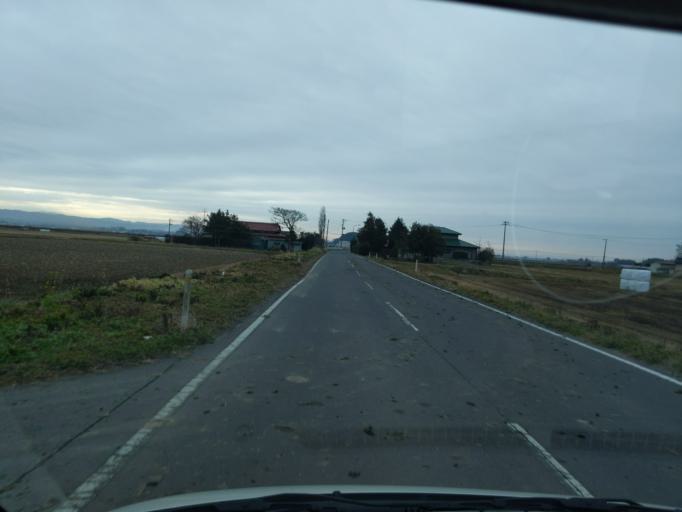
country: JP
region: Iwate
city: Ichinoseki
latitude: 38.7406
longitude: 141.2261
